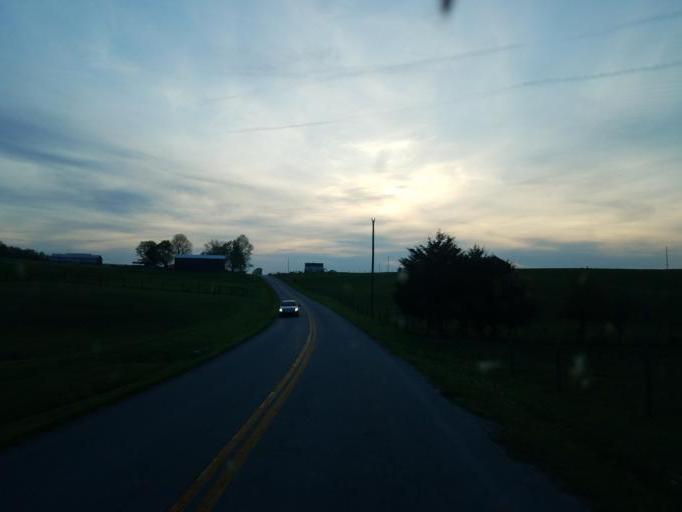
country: US
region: Kentucky
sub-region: Hart County
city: Munfordville
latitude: 37.2502
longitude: -85.7642
